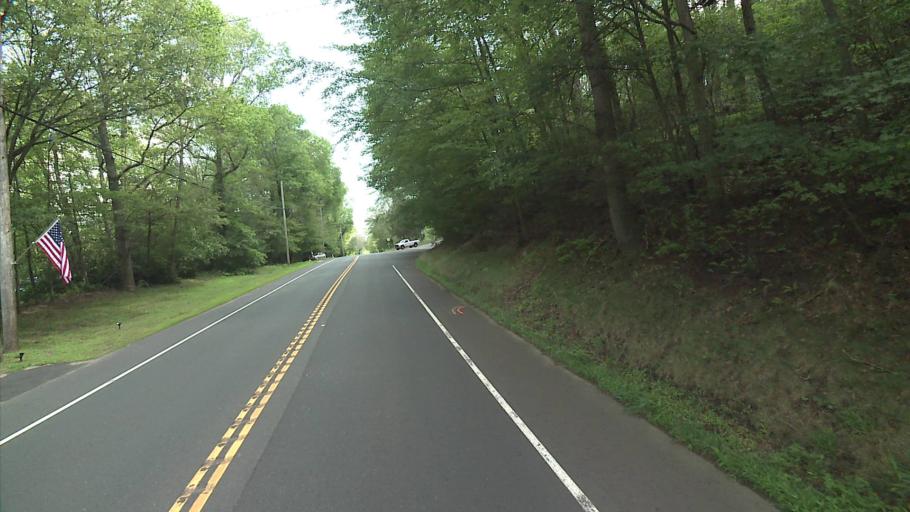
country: US
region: Connecticut
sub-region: Middlesex County
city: Higganum
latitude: 41.4967
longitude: -72.5419
